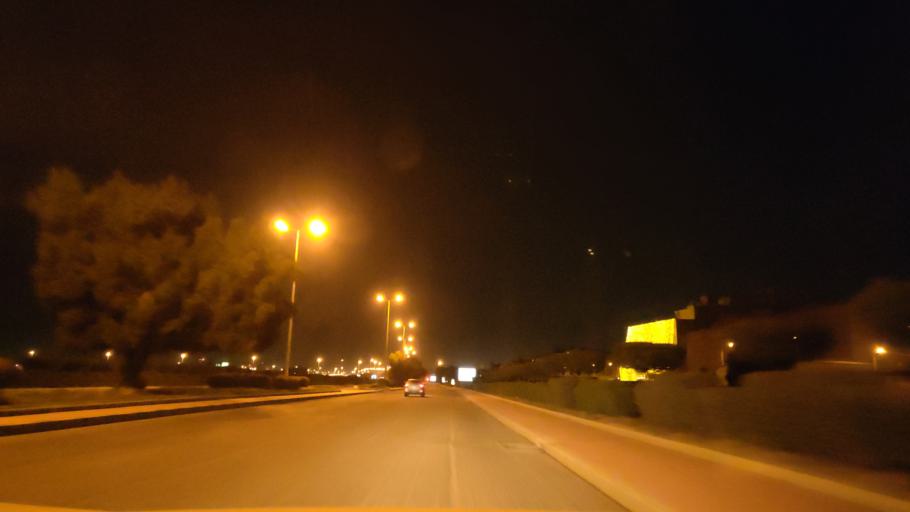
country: KW
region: Al Asimah
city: Ar Rabiyah
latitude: 29.2831
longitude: 47.9278
